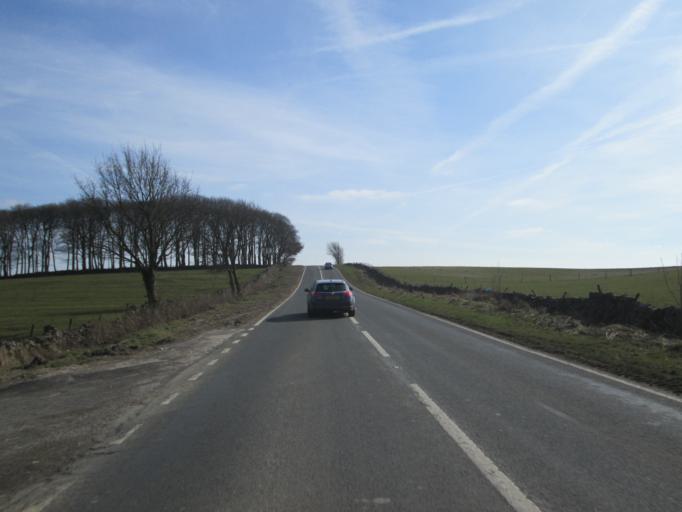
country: GB
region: England
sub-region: Derbyshire
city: Bakewell
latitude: 53.1574
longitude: -1.7719
